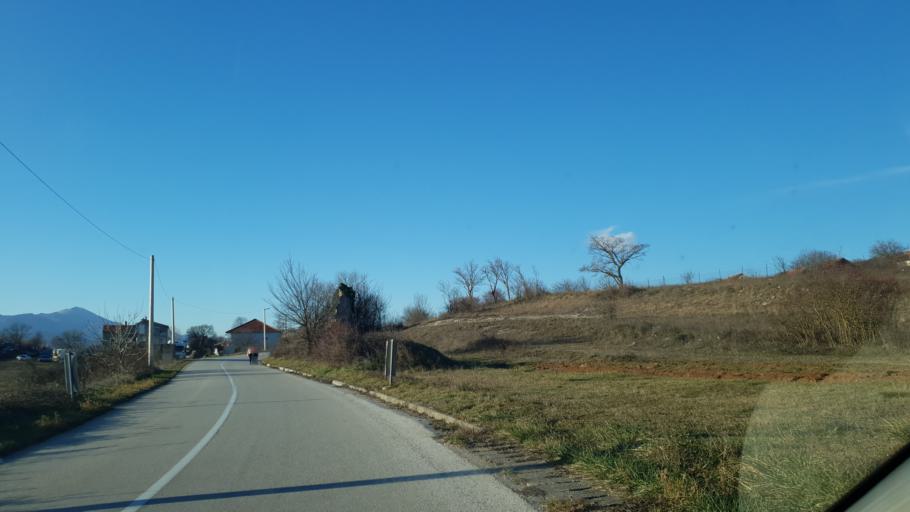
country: HR
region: Splitsko-Dalmatinska
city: Gala
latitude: 43.7356
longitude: 16.6851
